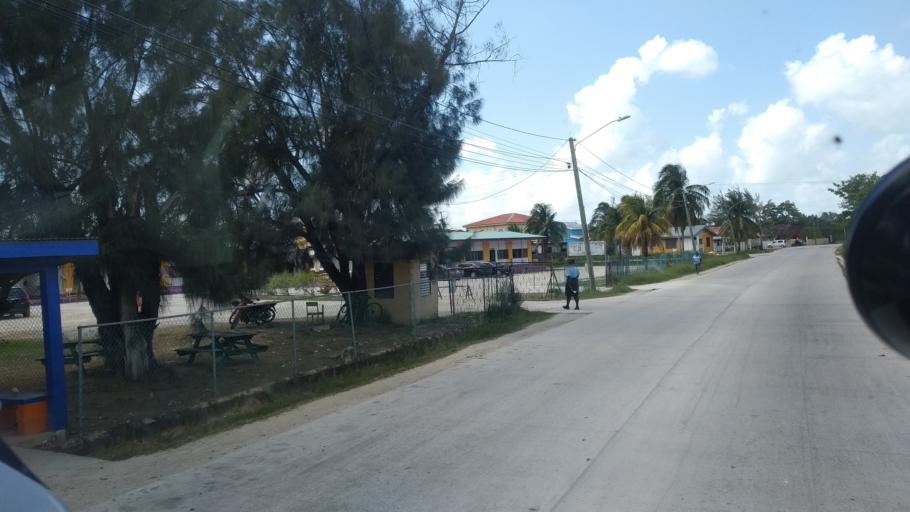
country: BZ
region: Belize
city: Belize City
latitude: 17.5116
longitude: -88.2002
